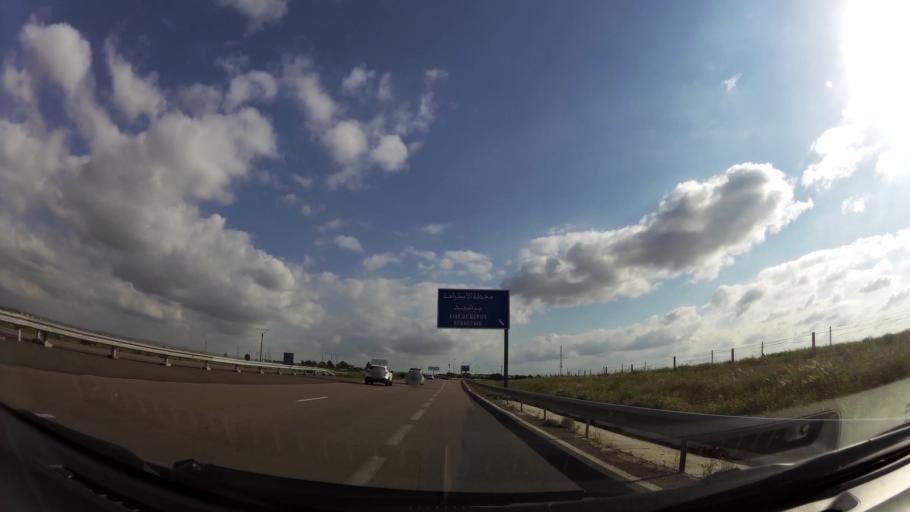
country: MA
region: Chaouia-Ouardigha
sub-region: Settat Province
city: Berrechid
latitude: 33.2276
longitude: -7.5734
